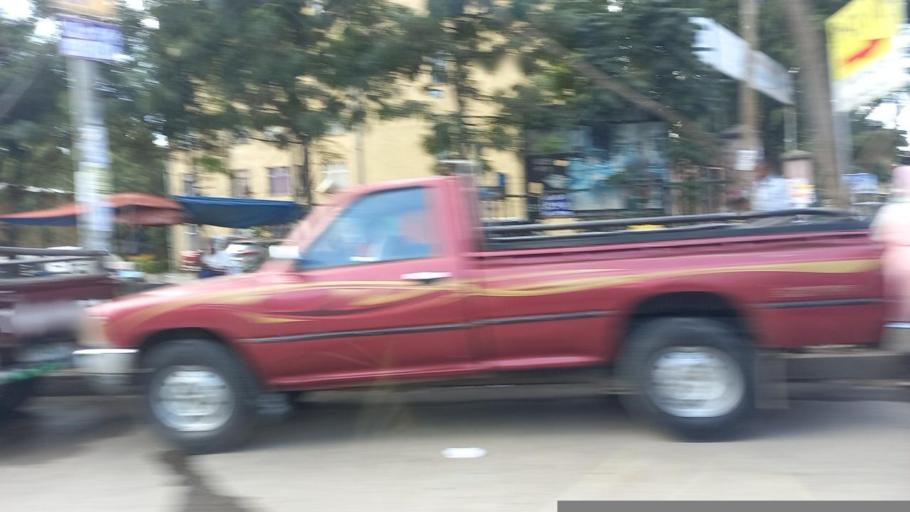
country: ET
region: Adis Abeba
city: Addis Ababa
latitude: 8.9580
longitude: 38.7122
